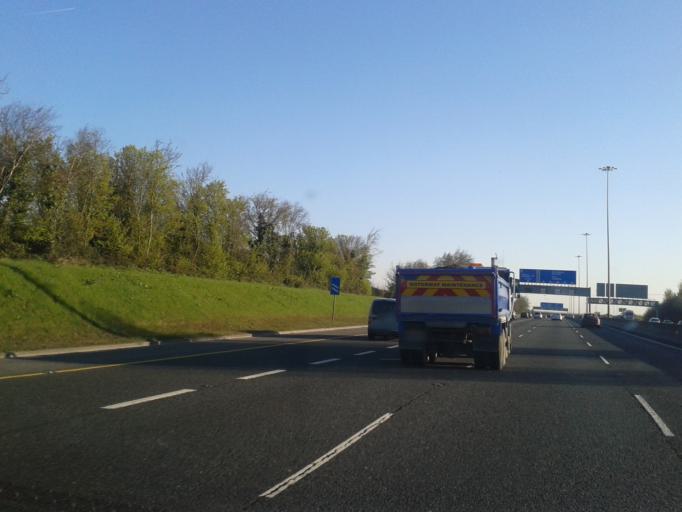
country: IE
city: Bonnybrook
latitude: 53.4197
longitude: -6.2216
